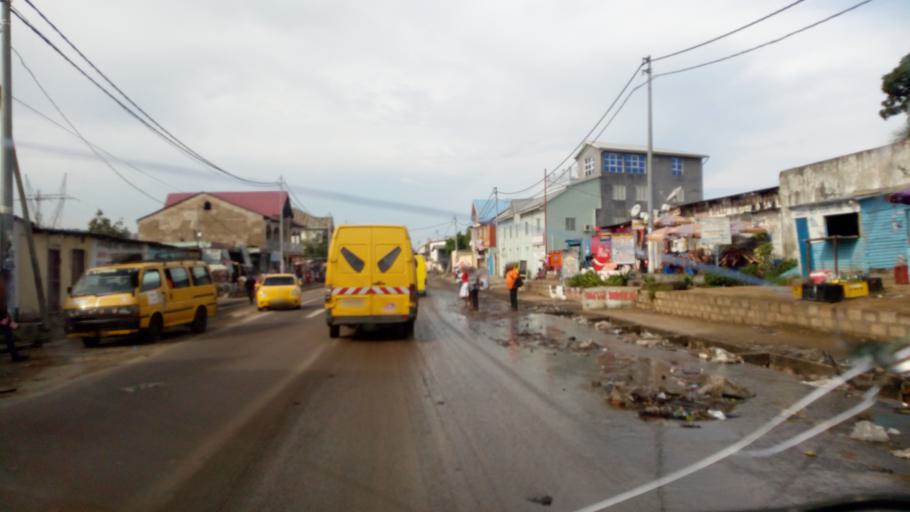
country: CD
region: Kinshasa
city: Kinshasa
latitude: -4.4389
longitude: 15.2572
